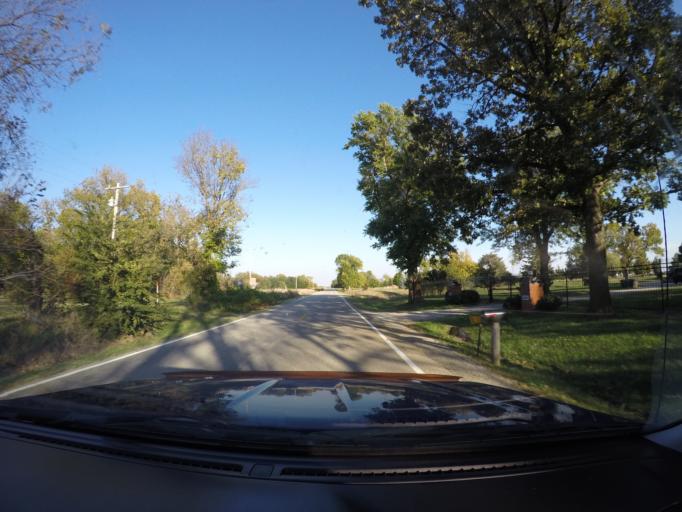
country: US
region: Kansas
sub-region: Saline County
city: Salina
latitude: 38.8416
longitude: -97.6723
